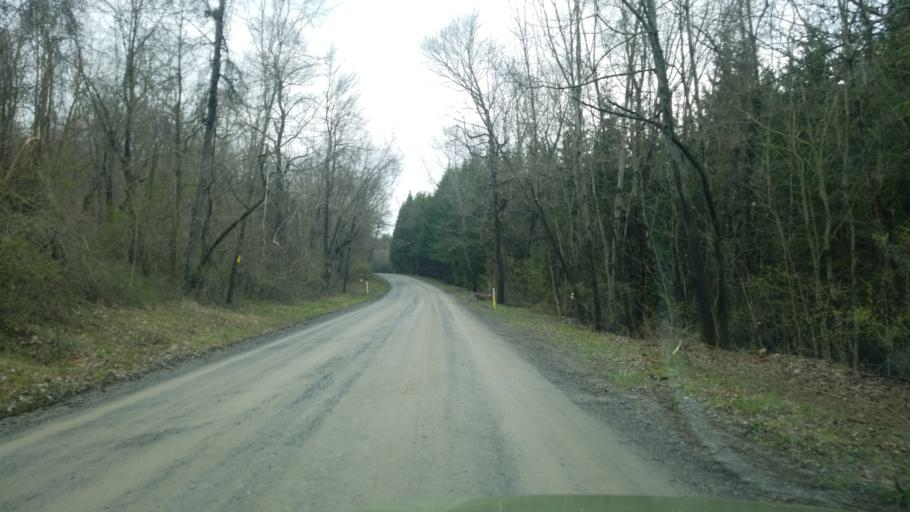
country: US
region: Pennsylvania
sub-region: Clearfield County
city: Shiloh
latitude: 41.1284
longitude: -78.3343
